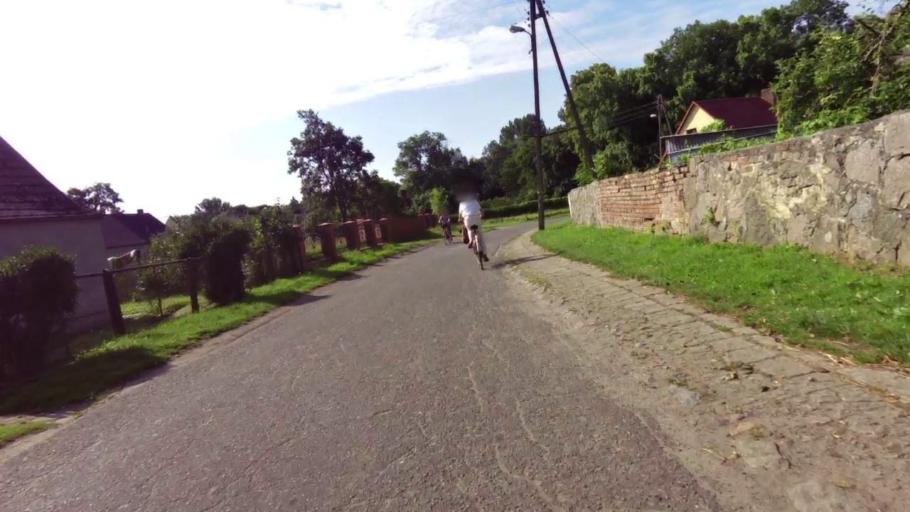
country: PL
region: West Pomeranian Voivodeship
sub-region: Powiat stargardzki
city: Marianowo
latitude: 53.3415
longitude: 15.1946
